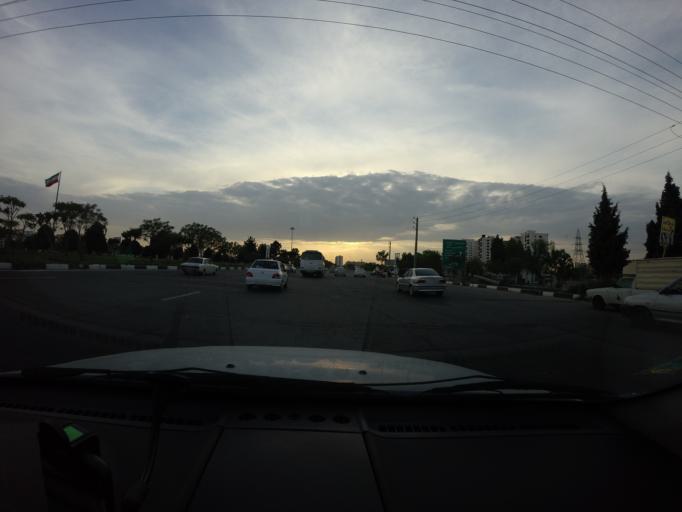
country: IR
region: Tehran
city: Eslamshahr
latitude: 35.5171
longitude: 51.2275
